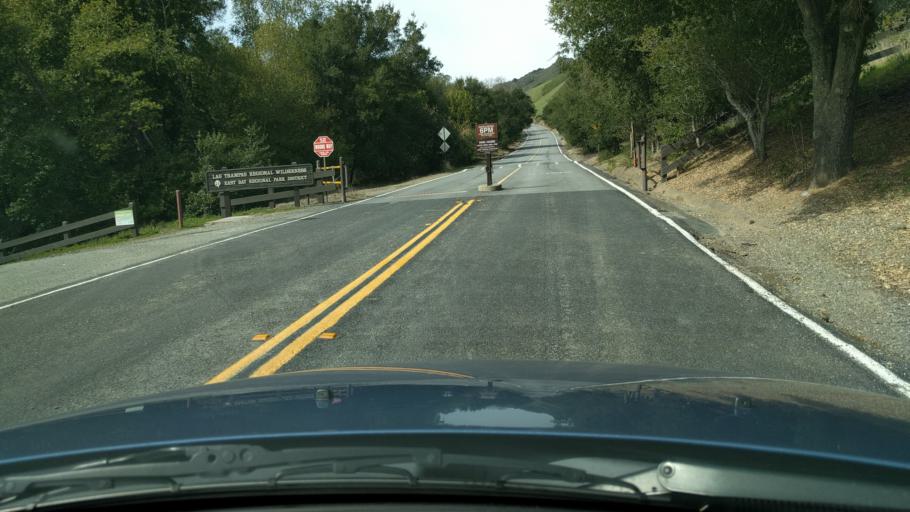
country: US
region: California
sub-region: Contra Costa County
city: Alamo
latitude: 37.8121
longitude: -122.0437
